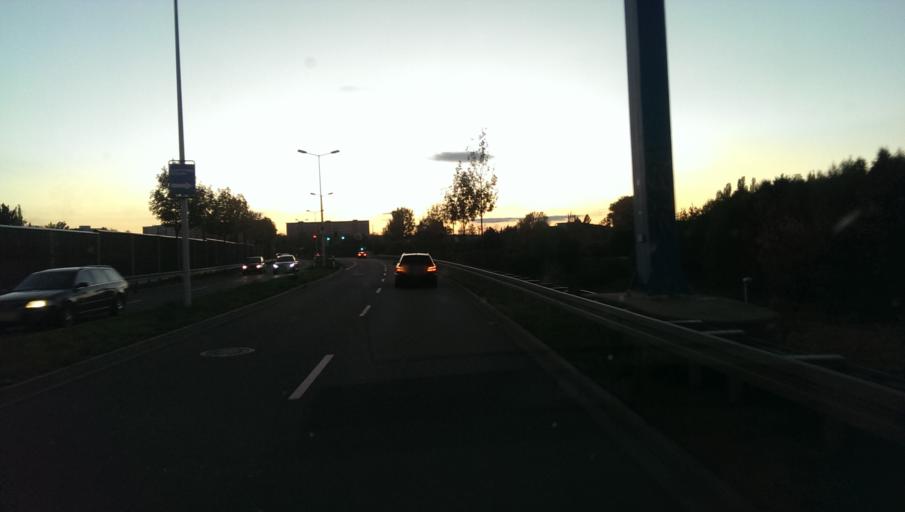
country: DE
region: Saxony
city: Hilbersdorf
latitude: 50.8189
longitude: 12.9683
